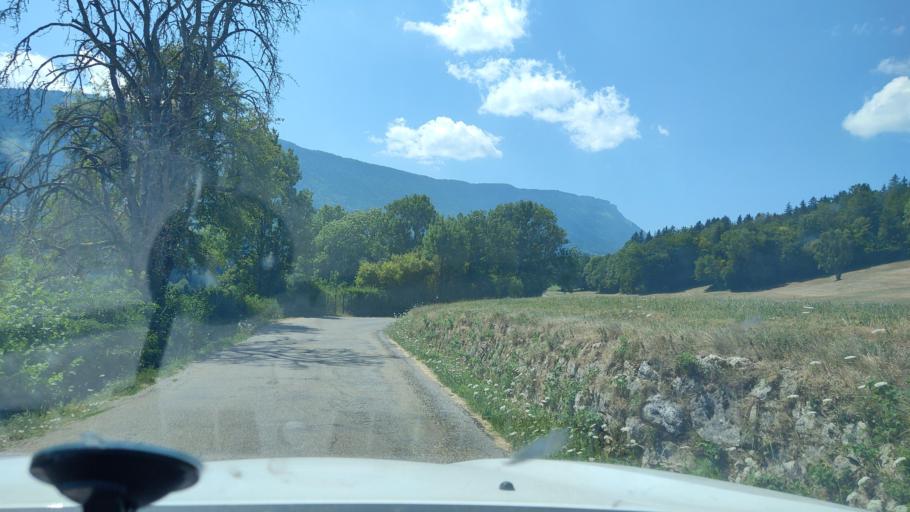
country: FR
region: Rhone-Alpes
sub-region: Departement de la Haute-Savoie
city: Cusy
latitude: 45.7069
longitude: 6.0806
